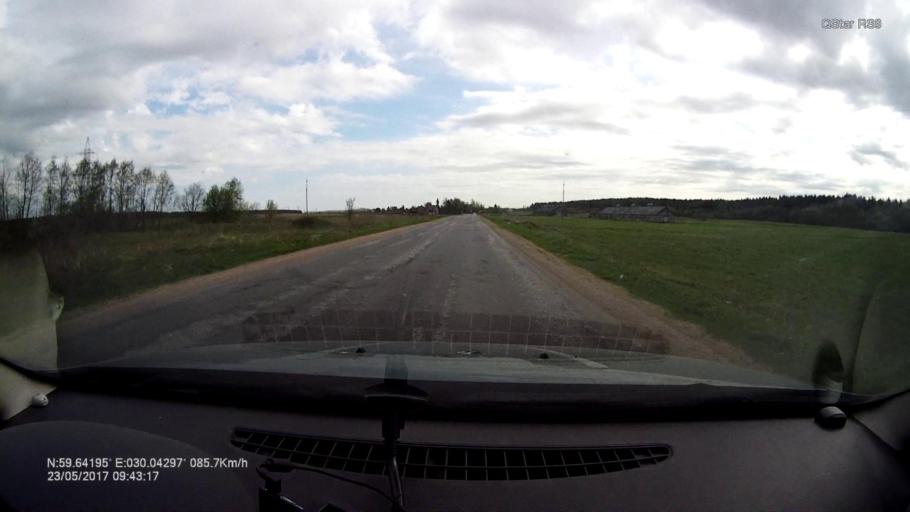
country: RU
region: Leningrad
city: Mariyenburg
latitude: 59.6422
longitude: 30.0436
